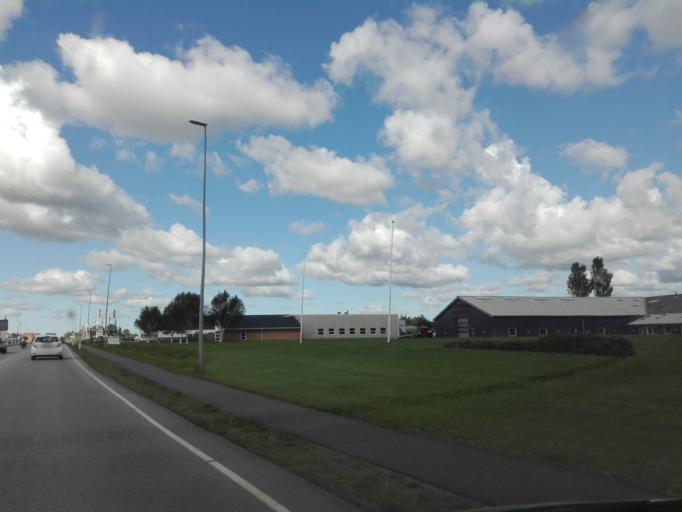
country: DK
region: North Denmark
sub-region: Mariagerfjord Kommune
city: Hobro
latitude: 56.6242
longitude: 9.8055
